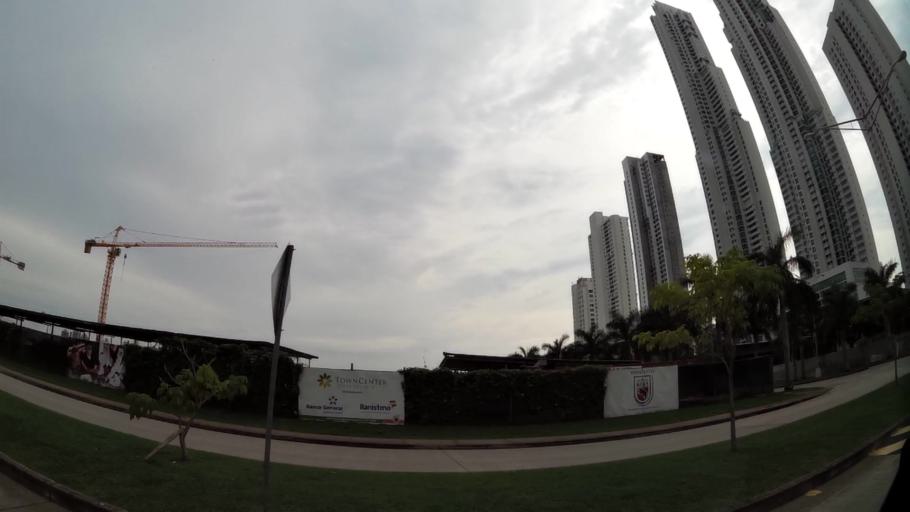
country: PA
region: Panama
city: San Miguelito
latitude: 9.0120
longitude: -79.4656
